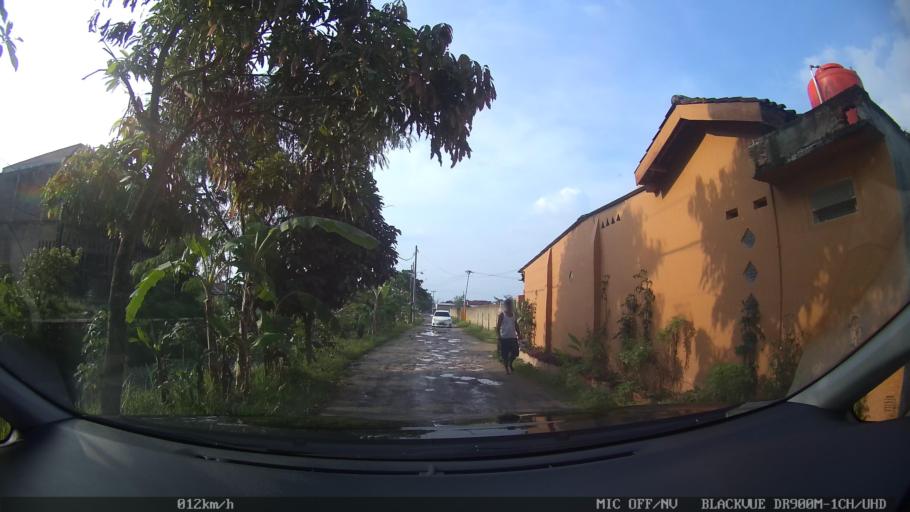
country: ID
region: Lampung
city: Kedaton
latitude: -5.3917
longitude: 105.3085
